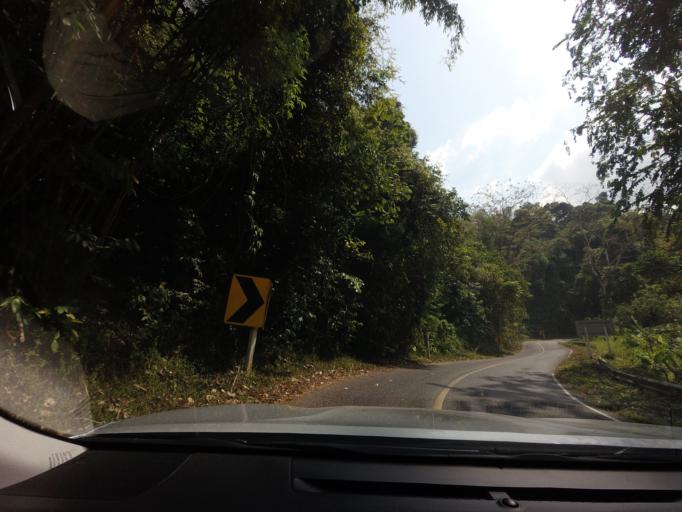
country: TH
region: Phangnga
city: Phang Nga
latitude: 8.5374
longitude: 98.5417
